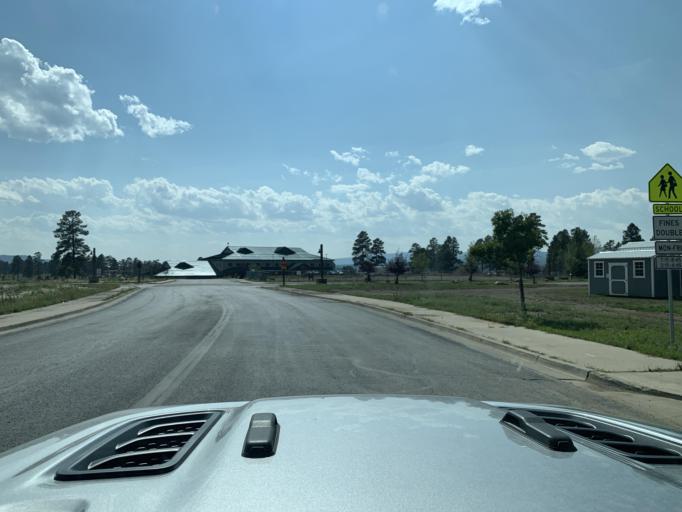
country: US
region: Colorado
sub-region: Archuleta County
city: Pagosa Springs
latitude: 37.2624
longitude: -107.0601
